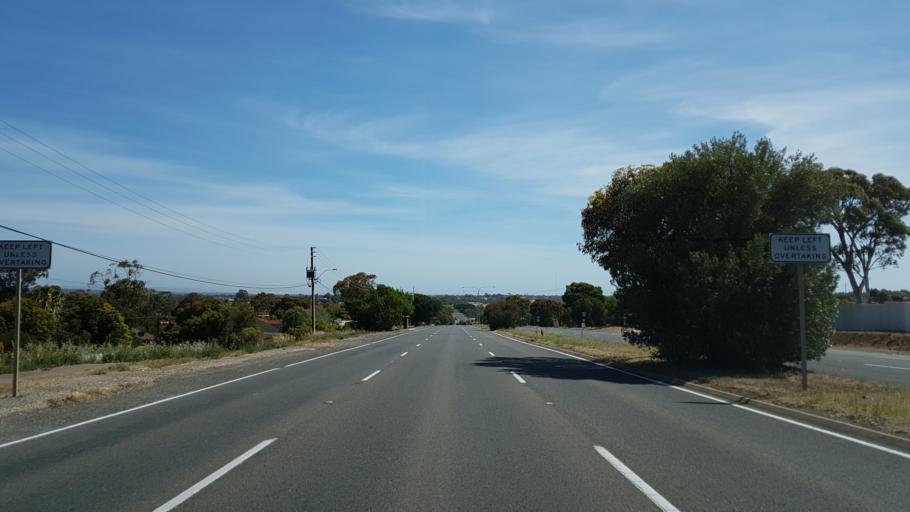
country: AU
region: South Australia
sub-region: Marion
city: Trott Park
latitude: -35.0727
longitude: 138.5528
